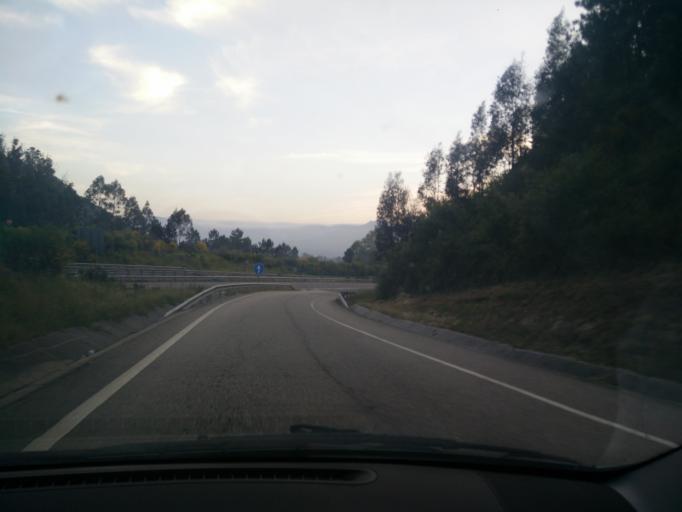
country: ES
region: Galicia
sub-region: Provincia de Pontevedra
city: Porrino
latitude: 42.1723
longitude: -8.5814
